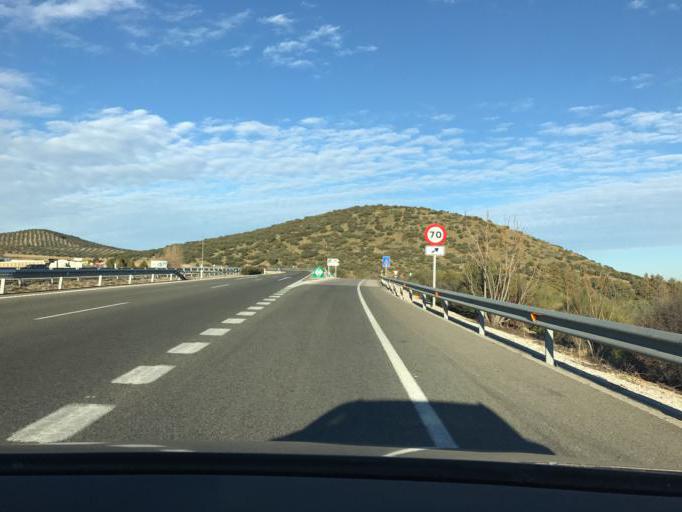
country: ES
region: Andalusia
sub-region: Provincia de Granada
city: Iznalloz
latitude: 37.4039
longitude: -3.5666
